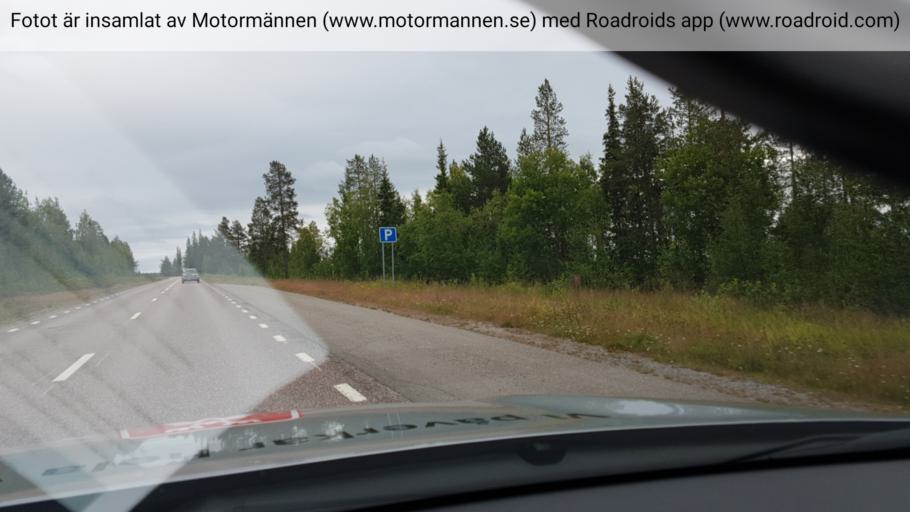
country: SE
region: Norrbotten
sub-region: Gallivare Kommun
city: Gaellivare
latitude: 67.0485
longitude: 21.6115
